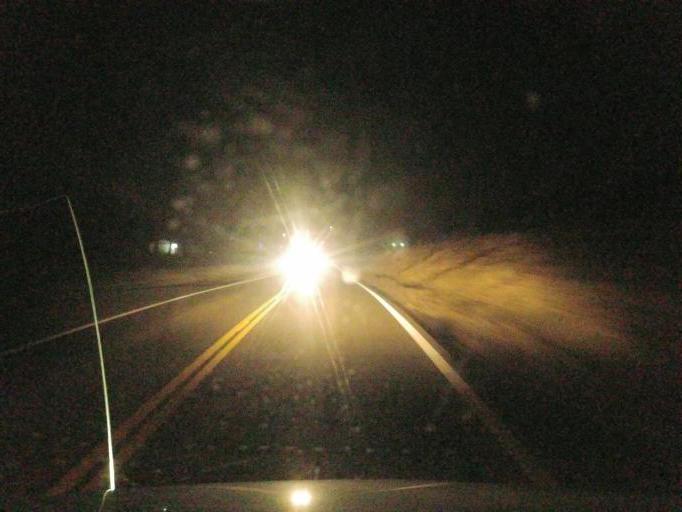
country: US
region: Ohio
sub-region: Carroll County
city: Carrollton
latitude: 40.4145
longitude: -81.1237
